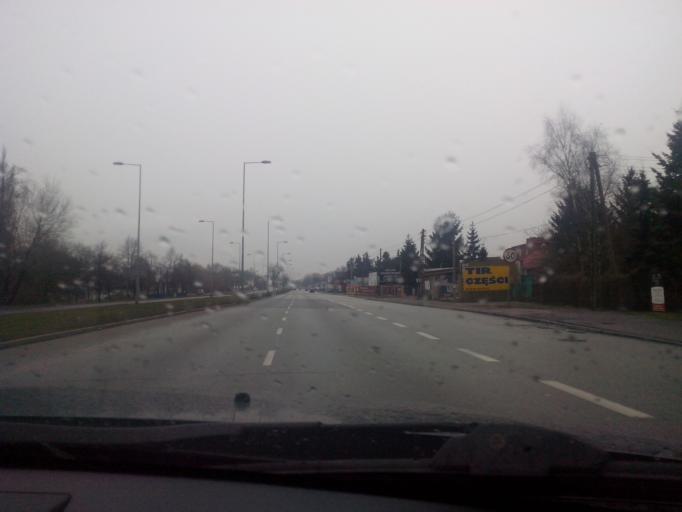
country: PL
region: Masovian Voivodeship
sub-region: Warszawa
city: Bialoleka
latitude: 52.3307
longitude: 20.9660
